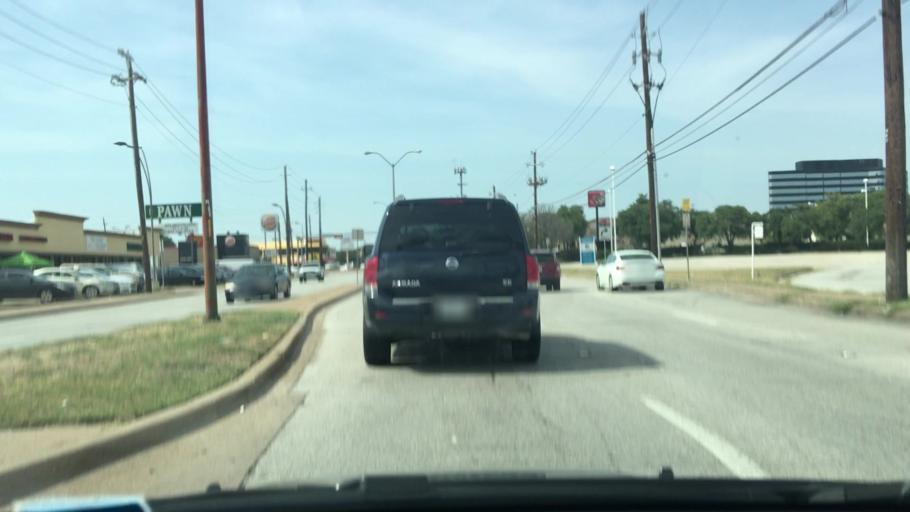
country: US
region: Texas
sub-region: Dallas County
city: Addison
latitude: 32.9292
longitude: -96.8113
